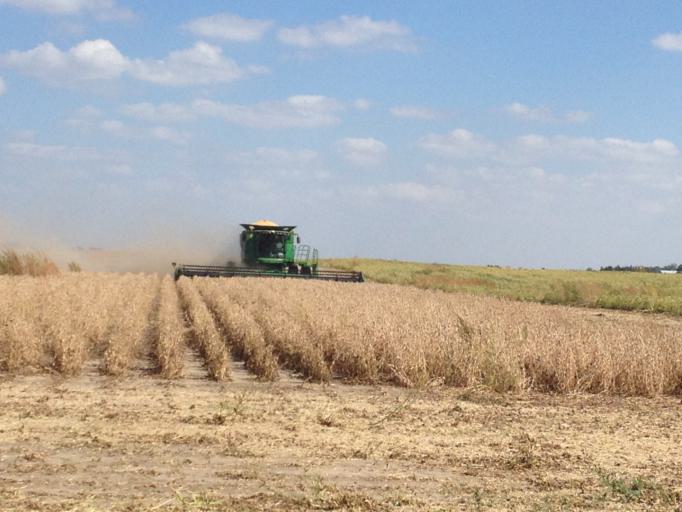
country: US
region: Kansas
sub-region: Barton County
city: Great Bend
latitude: 38.3087
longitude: -98.7745
